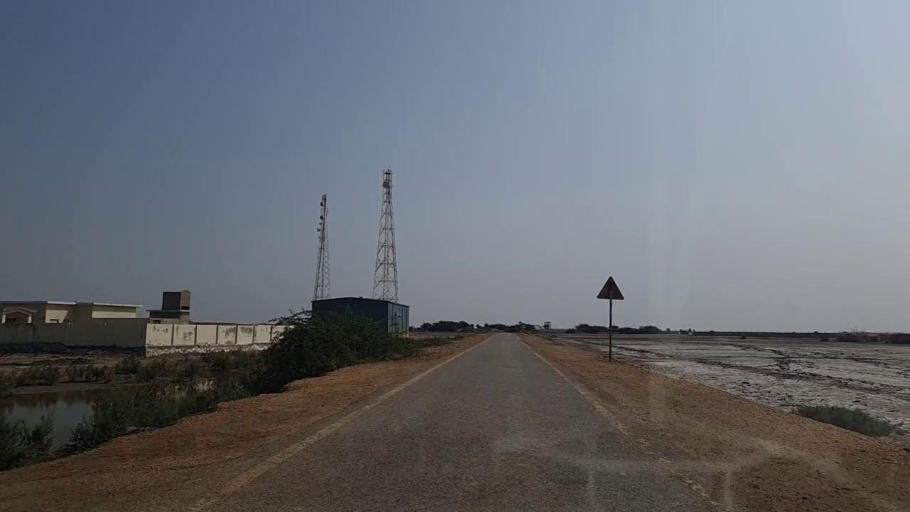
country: PK
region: Sindh
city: Chuhar Jamali
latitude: 24.1659
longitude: 67.8988
